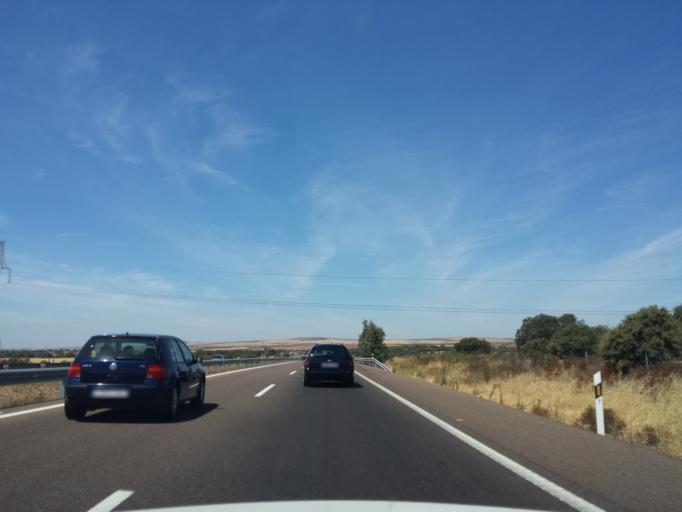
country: ES
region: Extremadura
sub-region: Provincia de Badajoz
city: Trujillanos
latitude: 38.9508
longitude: -6.2227
